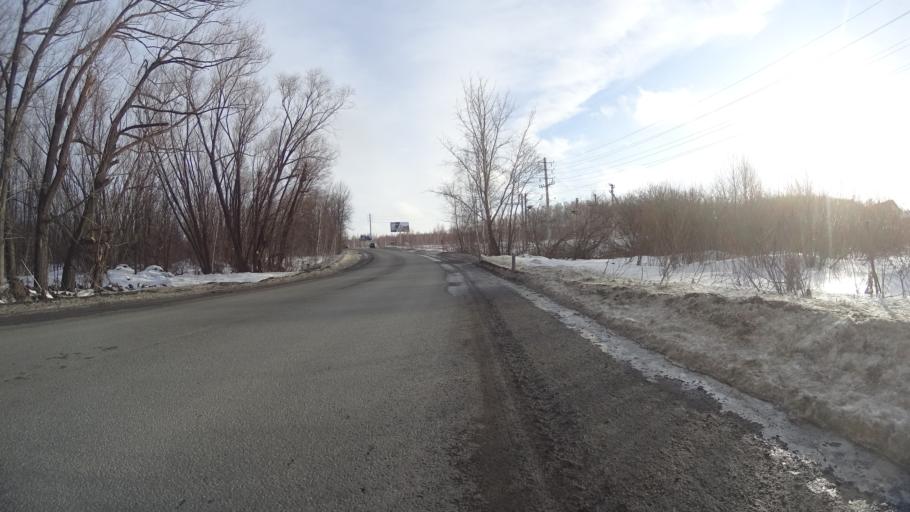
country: RU
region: Chelyabinsk
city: Sargazy
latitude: 55.1375
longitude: 61.2827
